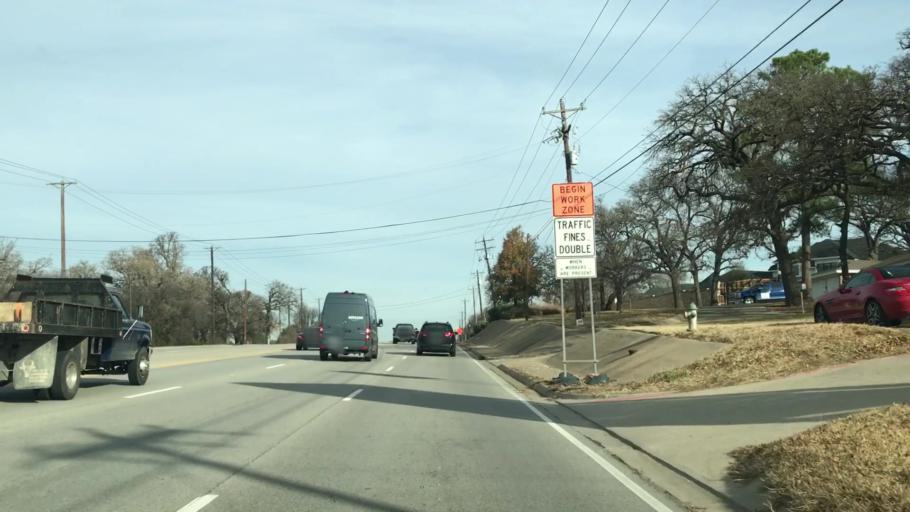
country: US
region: Texas
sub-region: Tarrant County
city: Southlake
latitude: 32.9297
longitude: -97.1858
